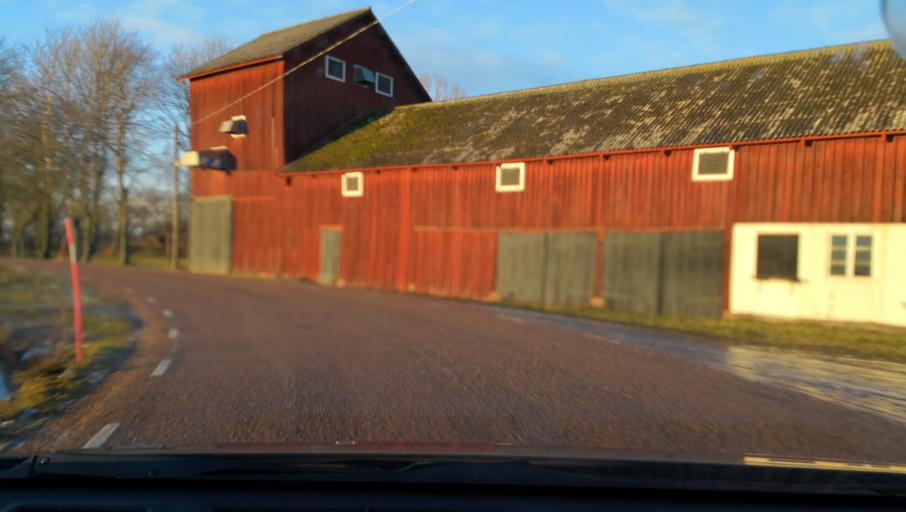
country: SE
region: Vaestmanland
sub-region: Vasteras
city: Tillberga
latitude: 59.6985
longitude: 16.5994
